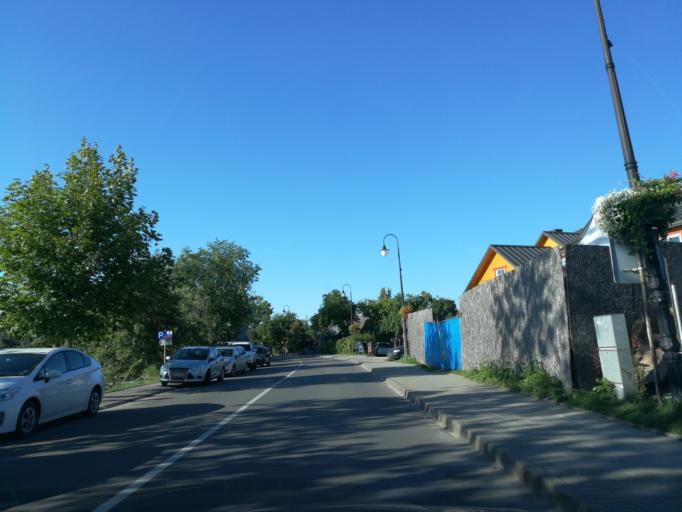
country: LT
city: Trakai
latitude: 54.6479
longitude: 24.9318
